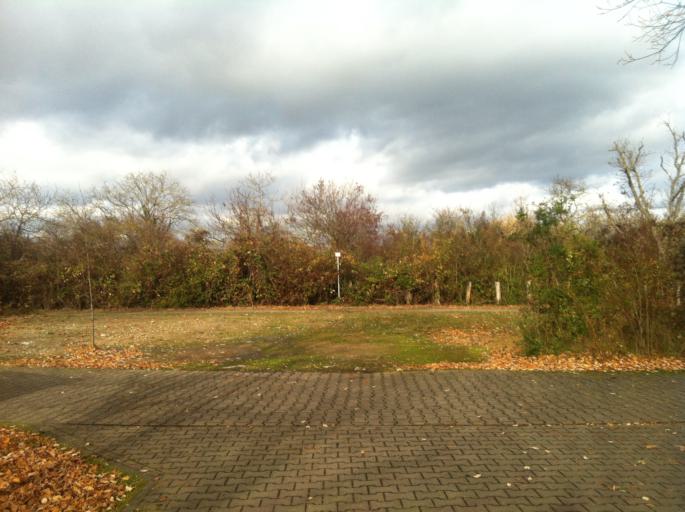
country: DE
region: Rheinland-Pfalz
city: Klein-Winternheim
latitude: 49.9947
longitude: 8.2223
